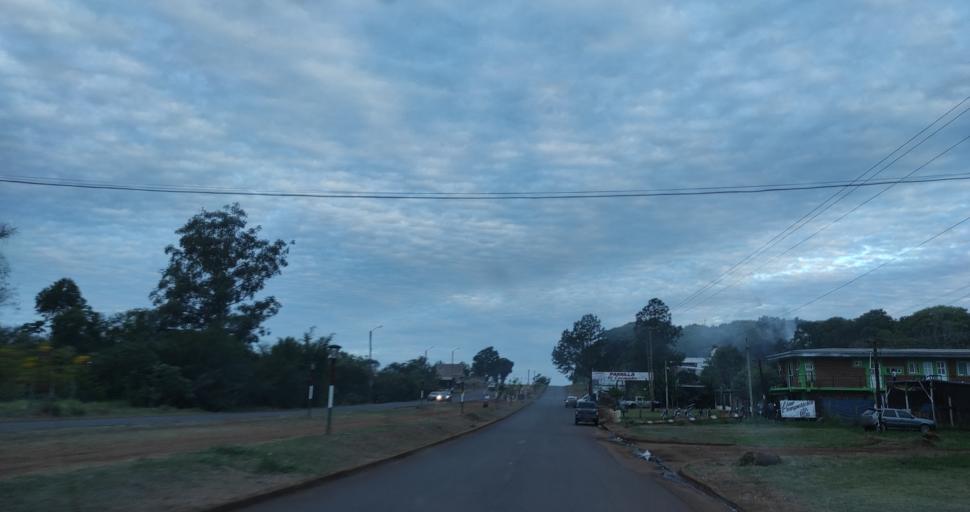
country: AR
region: Misiones
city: Garupa
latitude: -27.4664
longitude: -55.8547
